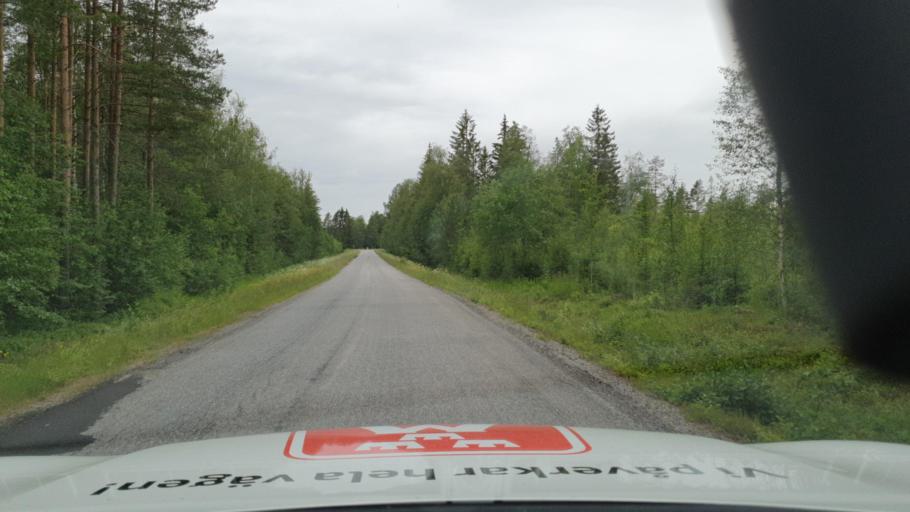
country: SE
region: Vaesterbotten
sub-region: Nordmalings Kommun
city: Nordmaling
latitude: 63.5286
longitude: 19.4171
